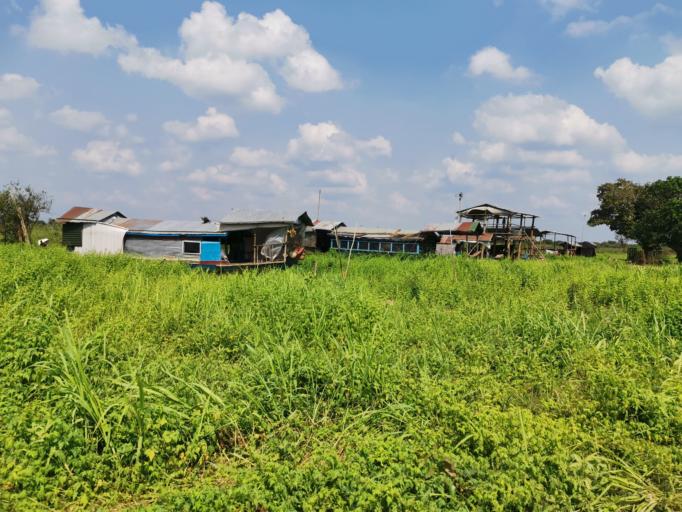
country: KH
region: Battambang
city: Battambang
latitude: 13.2857
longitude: 103.3700
